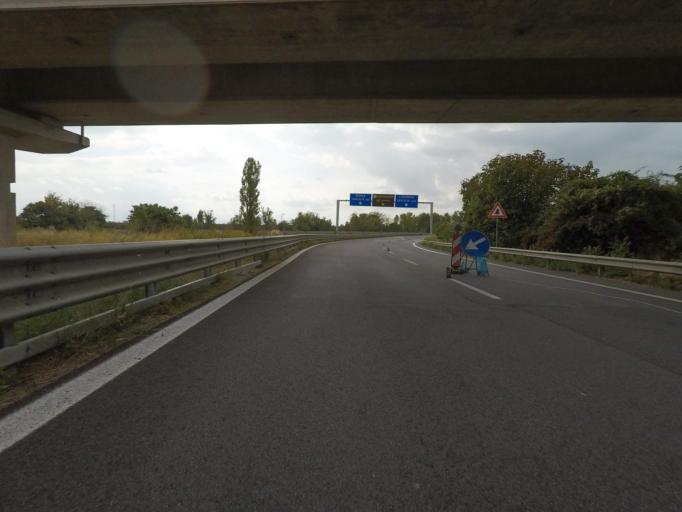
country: IT
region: Tuscany
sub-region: Provincia di Grosseto
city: Bagno Roselle
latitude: 42.7983
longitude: 11.1303
